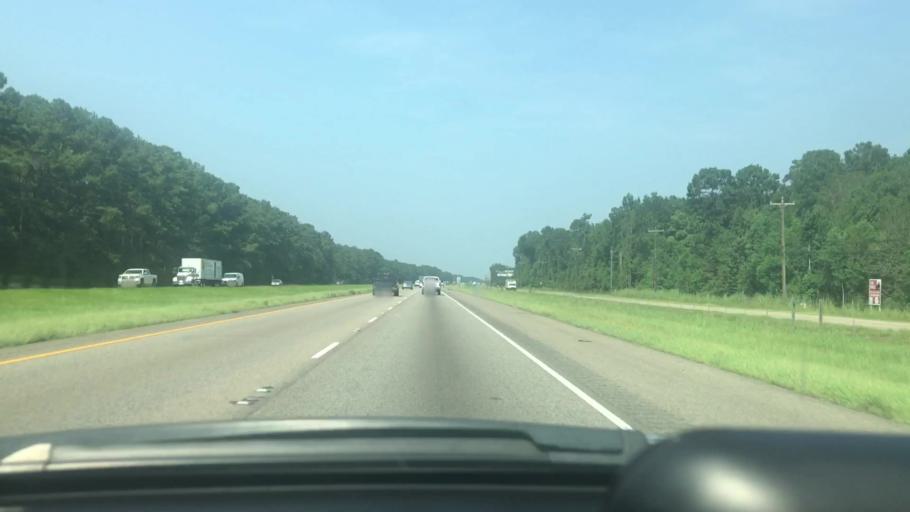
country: US
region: Louisiana
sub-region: Livingston Parish
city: Albany
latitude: 30.4755
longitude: -90.6098
